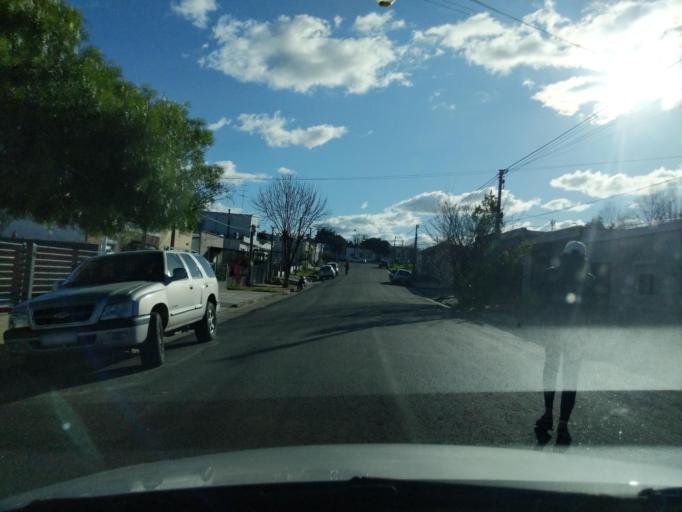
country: UY
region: Florida
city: Florida
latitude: -34.0904
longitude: -56.2137
